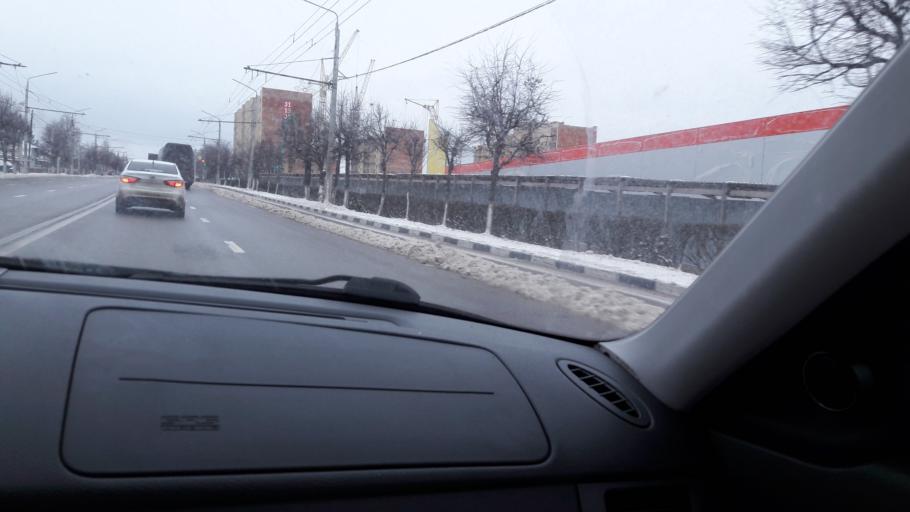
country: RU
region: Tula
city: Gorelki
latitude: 54.2319
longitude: 37.6254
